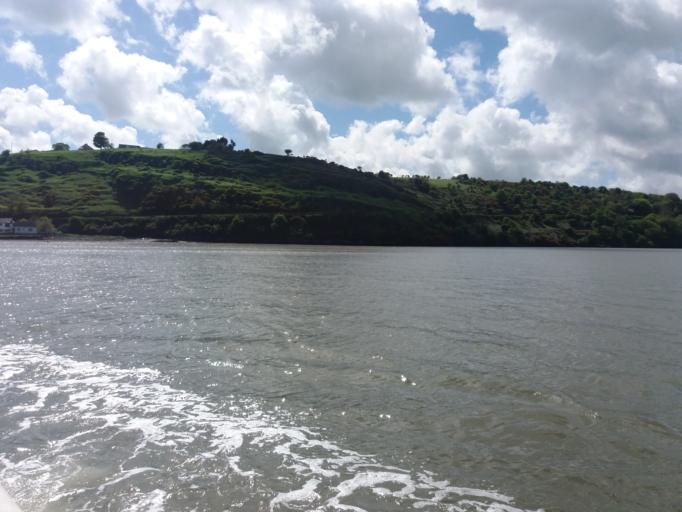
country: IE
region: Munster
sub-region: Waterford
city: Dunmore East
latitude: 52.2423
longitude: -6.9722
